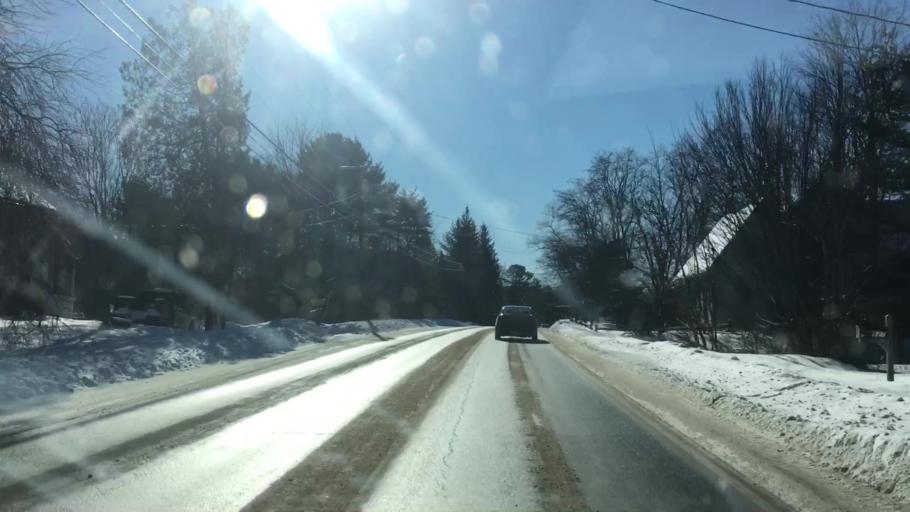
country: US
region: Maine
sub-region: Androscoggin County
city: Lisbon
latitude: 43.9777
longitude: -70.1243
